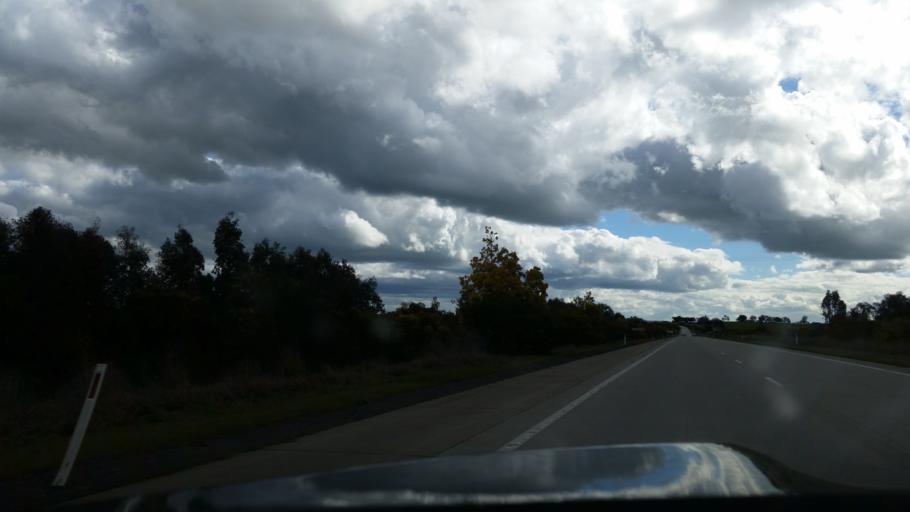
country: AU
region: New South Wales
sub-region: Greater Hume Shire
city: Jindera
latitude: -35.9265
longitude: 147.0722
